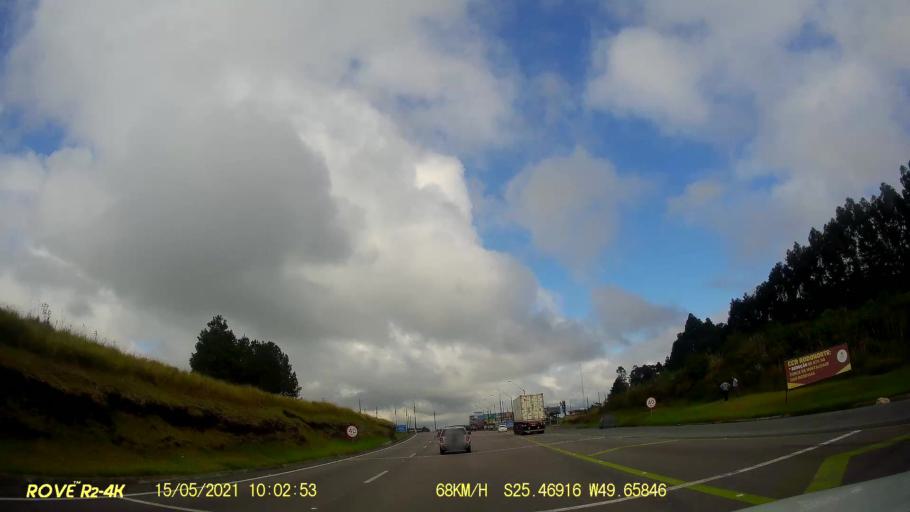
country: BR
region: Parana
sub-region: Campo Largo
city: Campo Largo
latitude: -25.4692
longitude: -49.6585
